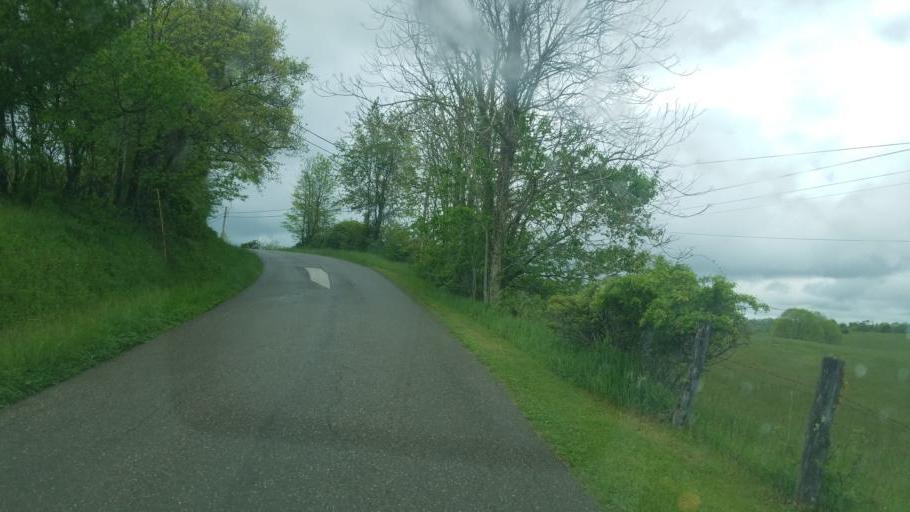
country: US
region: Ohio
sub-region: Tuscarawas County
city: Rockford
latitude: 40.4007
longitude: -81.1928
